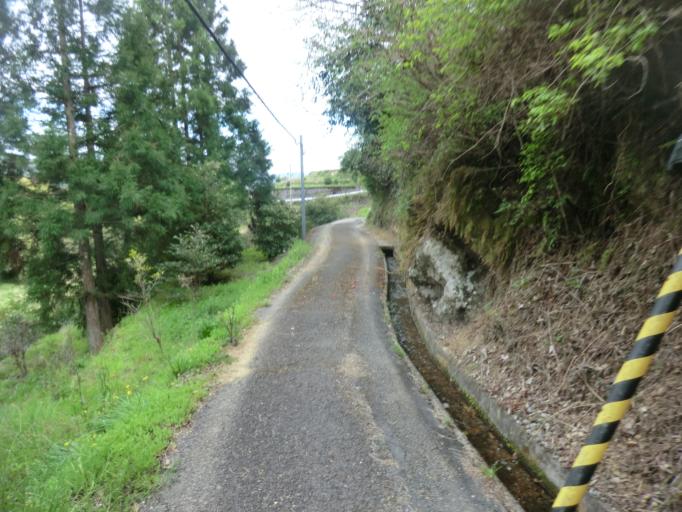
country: JP
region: Kochi
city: Kochi-shi
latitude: 33.6433
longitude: 133.7189
